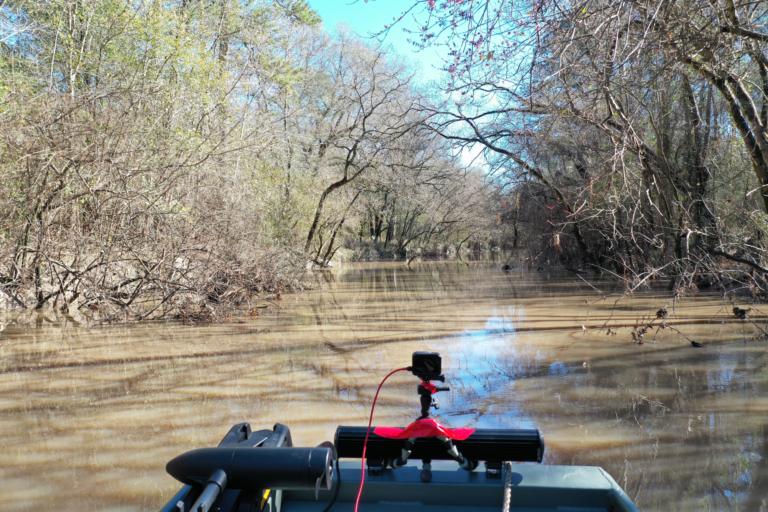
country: US
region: Louisiana
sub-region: Calcasieu Parish
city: Iowa
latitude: 30.3146
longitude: -93.0421
